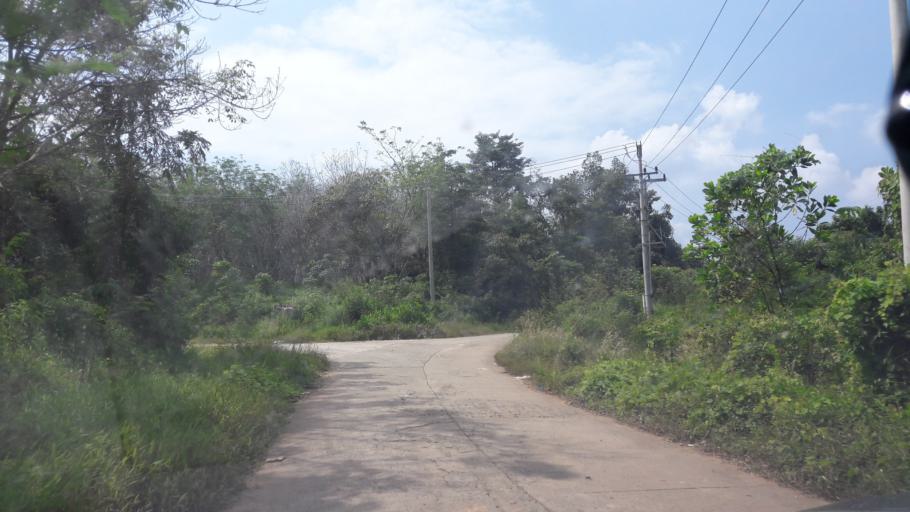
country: ID
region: South Sumatra
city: Gunungmegang Dalam
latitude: -3.2925
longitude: 103.8683
